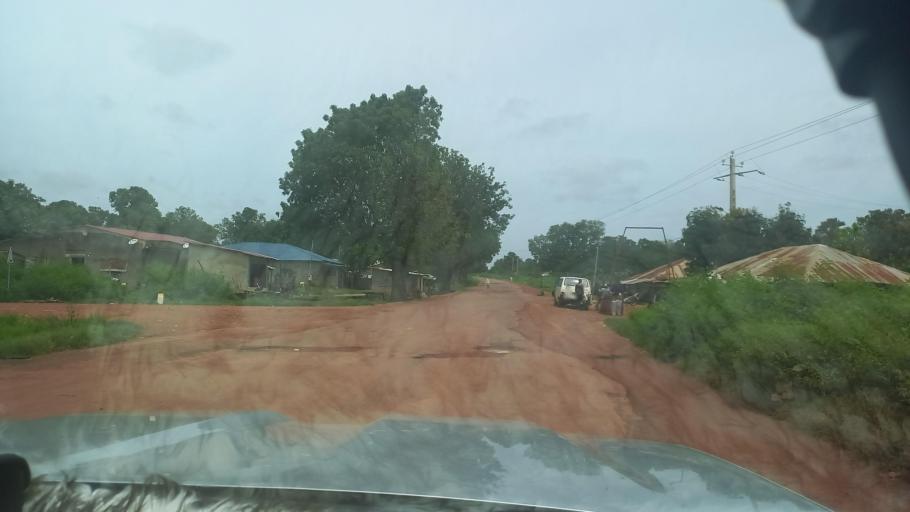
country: SN
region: Kolda
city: Marsassoum
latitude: 12.9141
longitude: -16.0100
